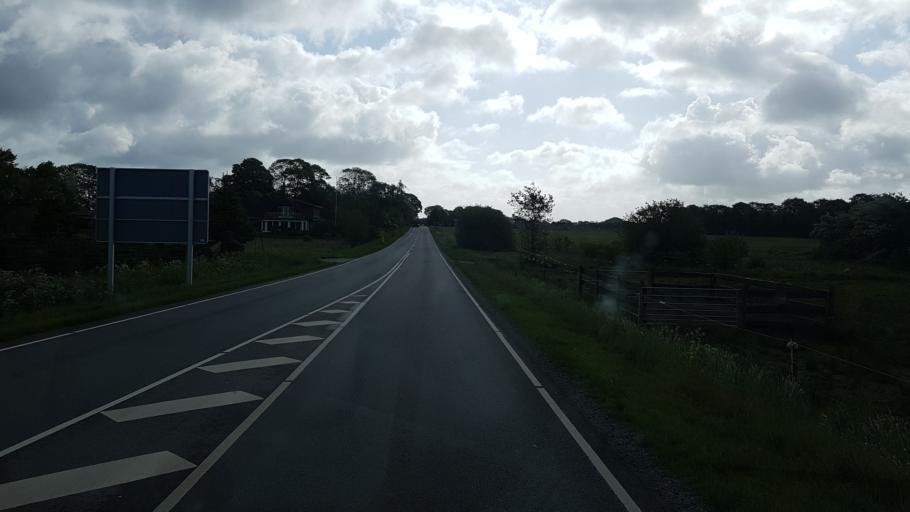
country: DK
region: South Denmark
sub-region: Vejen Kommune
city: Vejen
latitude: 55.4492
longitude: 9.1393
